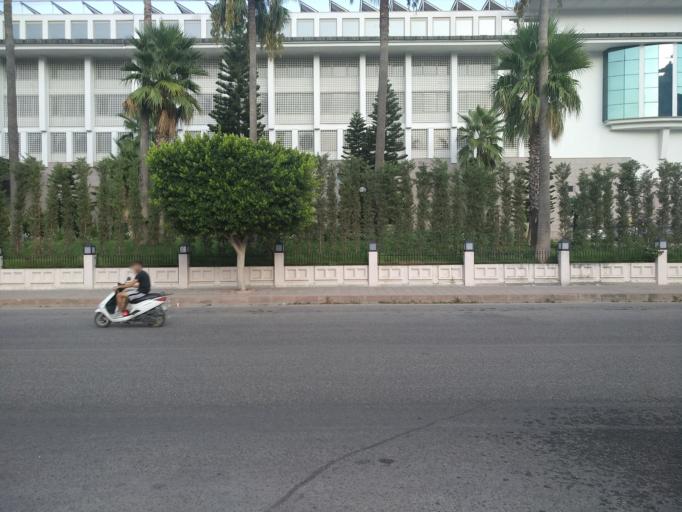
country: TR
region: Antalya
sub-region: Kemer
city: Goeynuek
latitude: 36.6634
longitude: 30.5599
